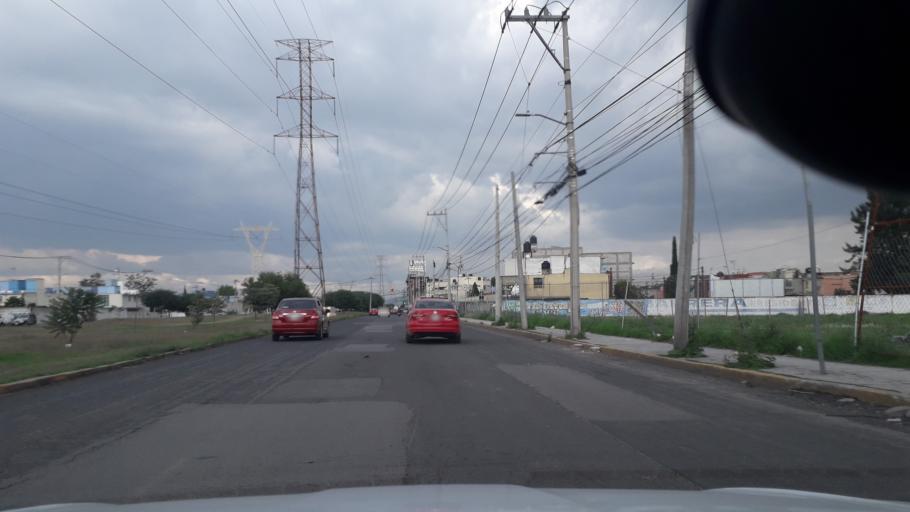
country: MX
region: Mexico
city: Santiago Teyahualco
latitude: 19.6415
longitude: -99.1183
